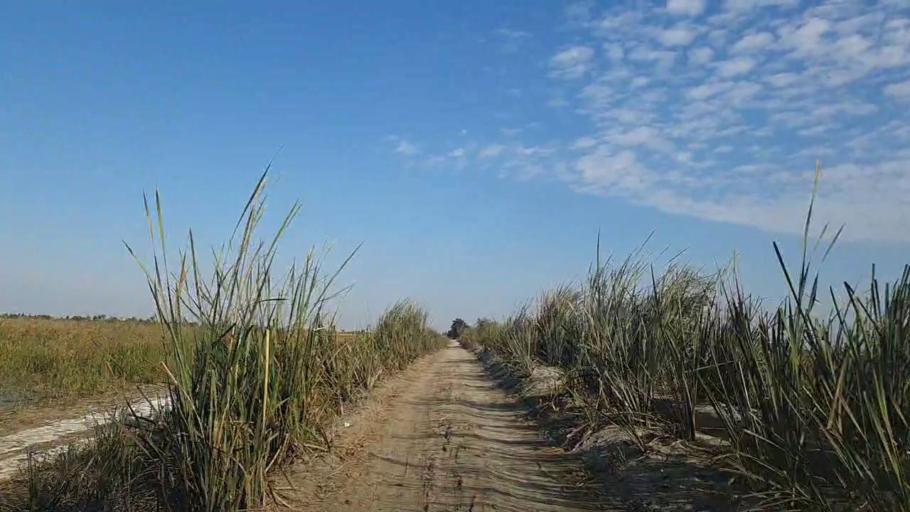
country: PK
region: Sindh
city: Khadro
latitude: 26.3024
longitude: 68.8316
